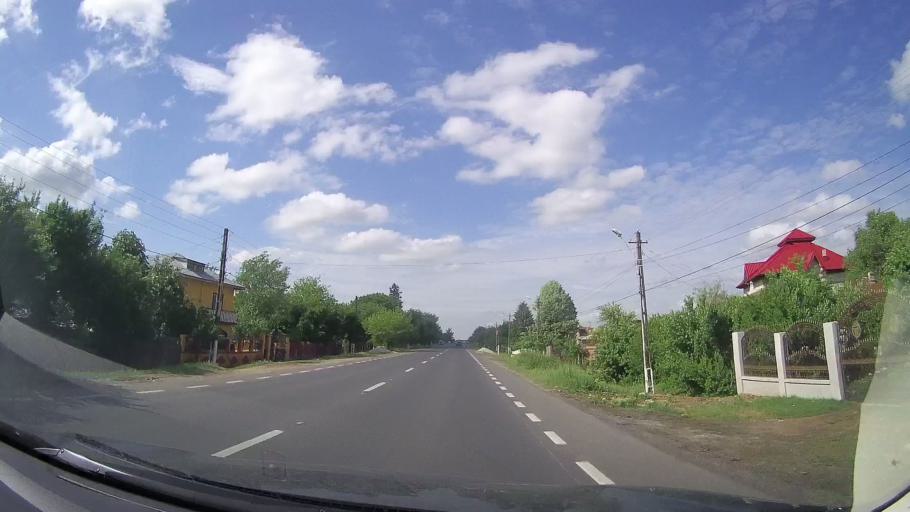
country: RO
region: Giurgiu
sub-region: Comuna Ghimpati
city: Ghimpati
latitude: 44.1991
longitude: 25.7885
